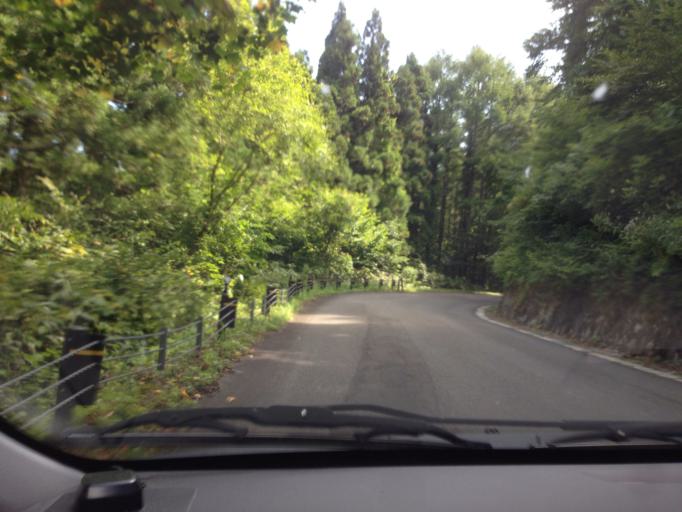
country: JP
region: Fukushima
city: Inawashiro
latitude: 37.3442
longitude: 140.0584
